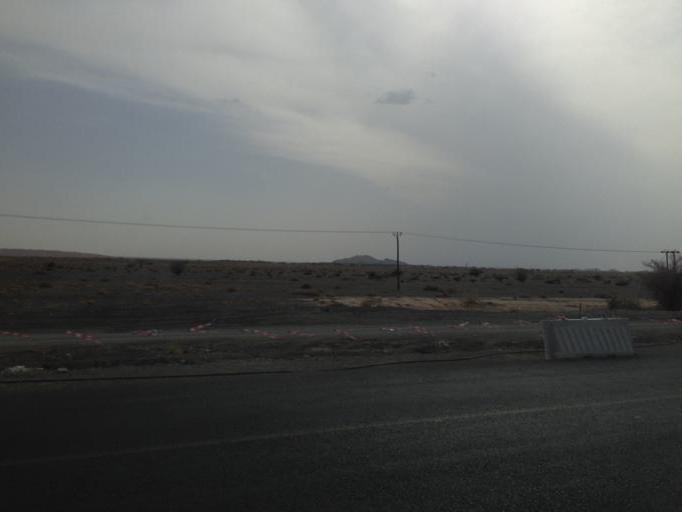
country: OM
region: Ash Sharqiyah
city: Al Qabil
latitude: 22.5515
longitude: 58.7177
